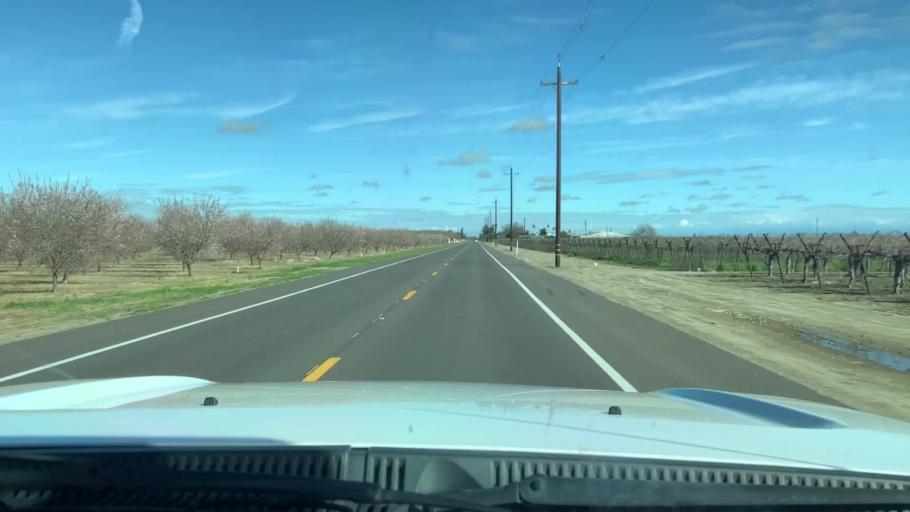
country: US
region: California
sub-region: Fresno County
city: Selma
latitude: 36.5214
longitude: -119.6829
